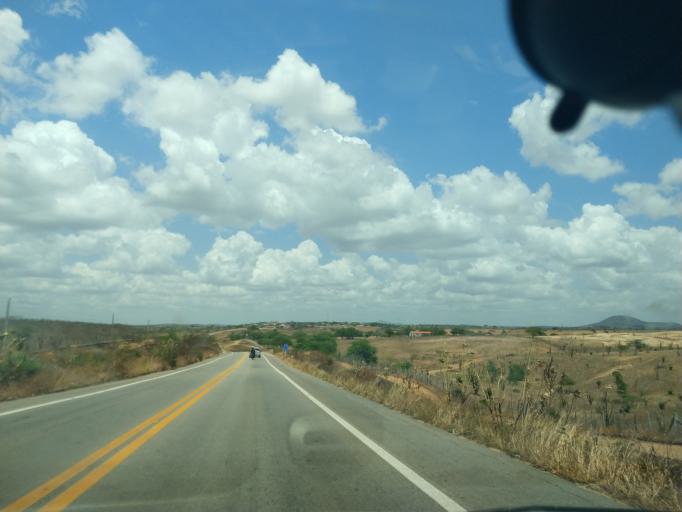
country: BR
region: Rio Grande do Norte
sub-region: Tangara
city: Tangara
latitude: -6.1832
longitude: -35.7746
